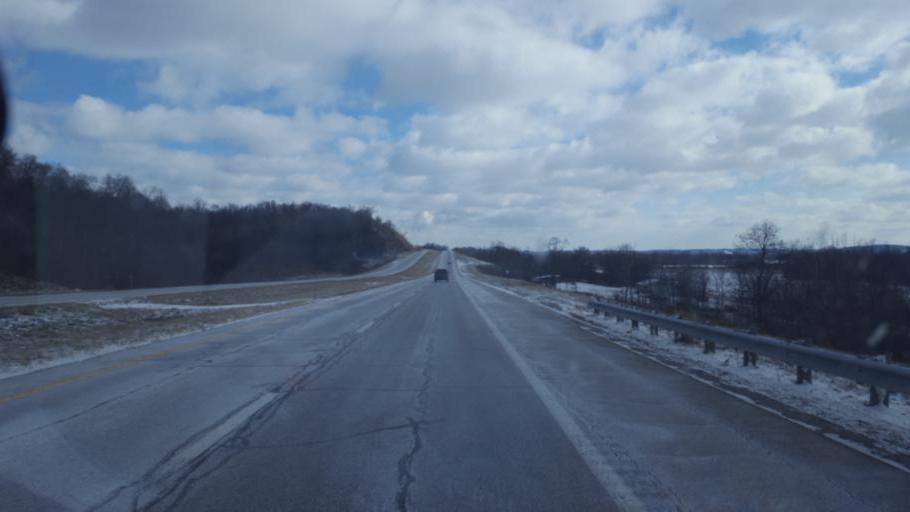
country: US
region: Ohio
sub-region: Muskingum County
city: Frazeysburg
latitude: 40.1504
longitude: -82.0679
